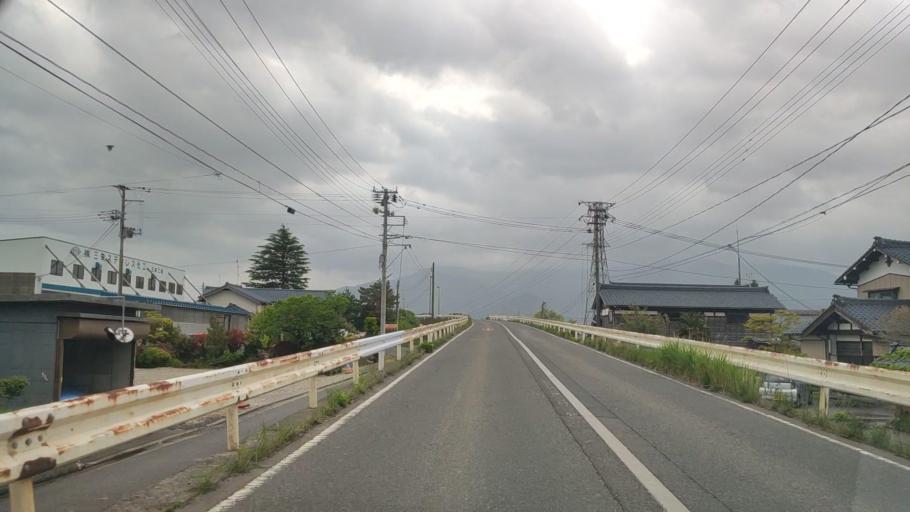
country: JP
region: Niigata
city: Gosen
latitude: 37.7331
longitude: 139.1998
